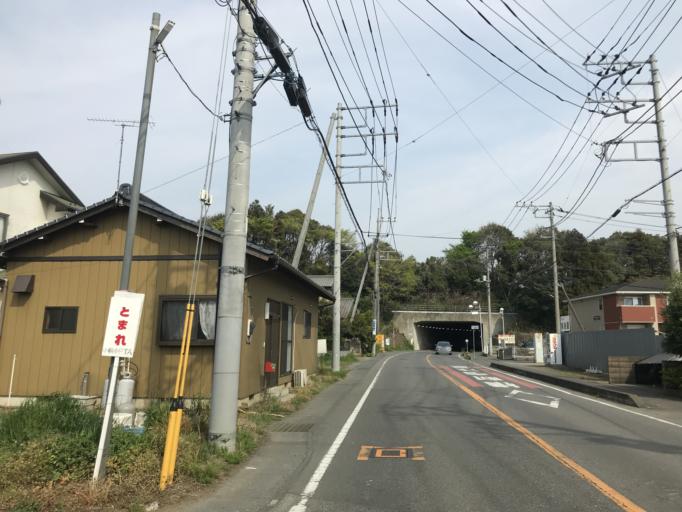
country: JP
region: Ibaraki
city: Moriya
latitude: 35.9733
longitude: 139.9861
